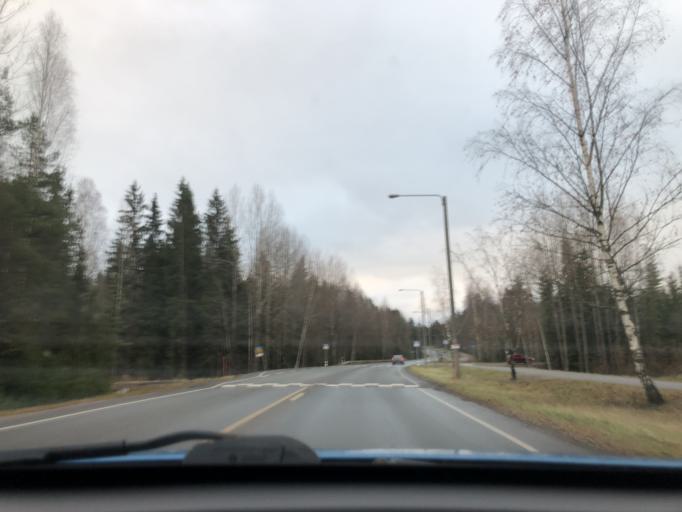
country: FI
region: Pirkanmaa
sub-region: Tampere
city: Kangasala
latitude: 61.5314
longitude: 23.9526
